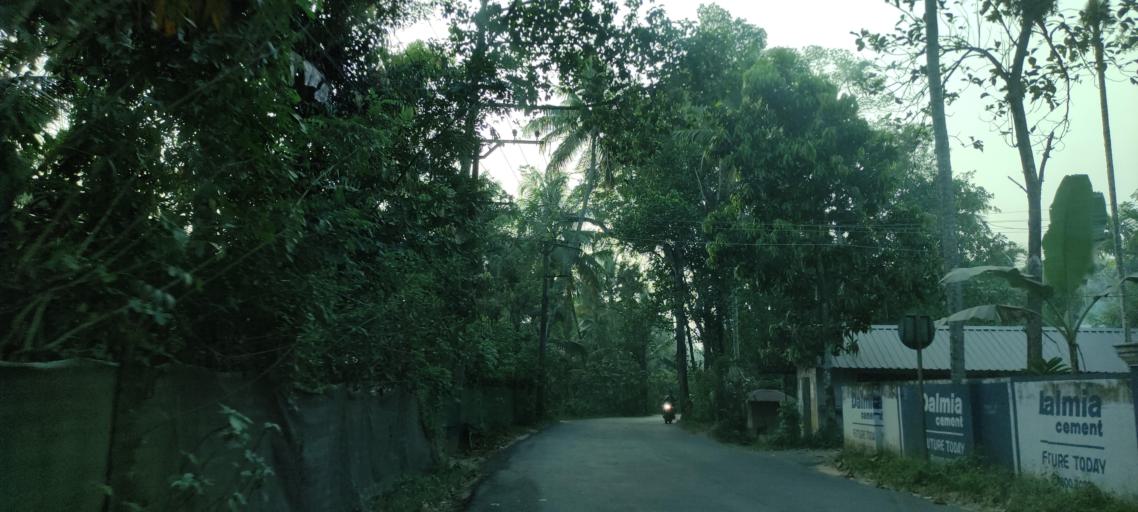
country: IN
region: Kerala
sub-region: Kottayam
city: Vaikam
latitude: 9.6867
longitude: 76.4227
